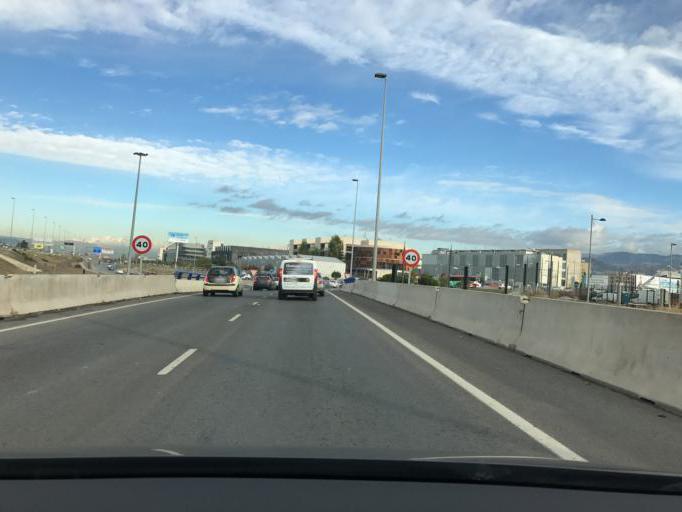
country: ES
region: Andalusia
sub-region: Provincia de Granada
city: Armilla
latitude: 37.1454
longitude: -3.6089
